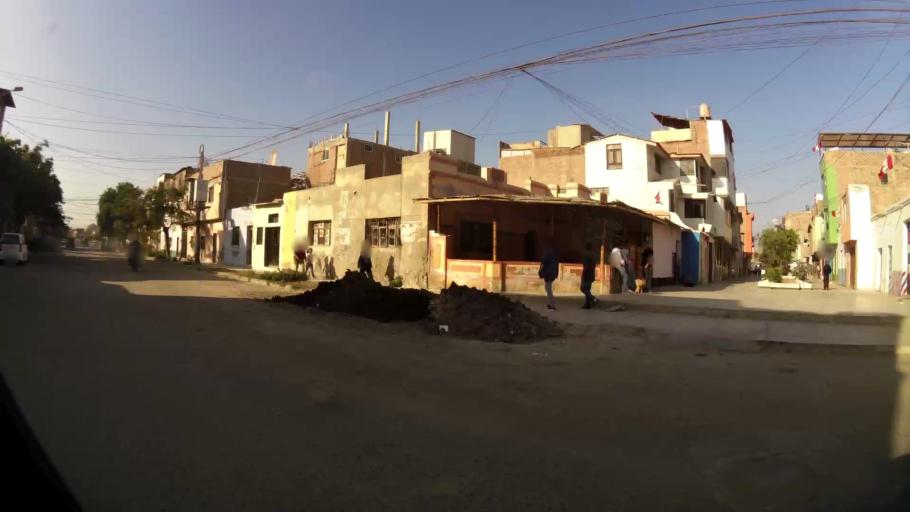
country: PE
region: Lambayeque
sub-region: Provincia de Chiclayo
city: Chiclayo
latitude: -6.7684
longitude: -79.8456
